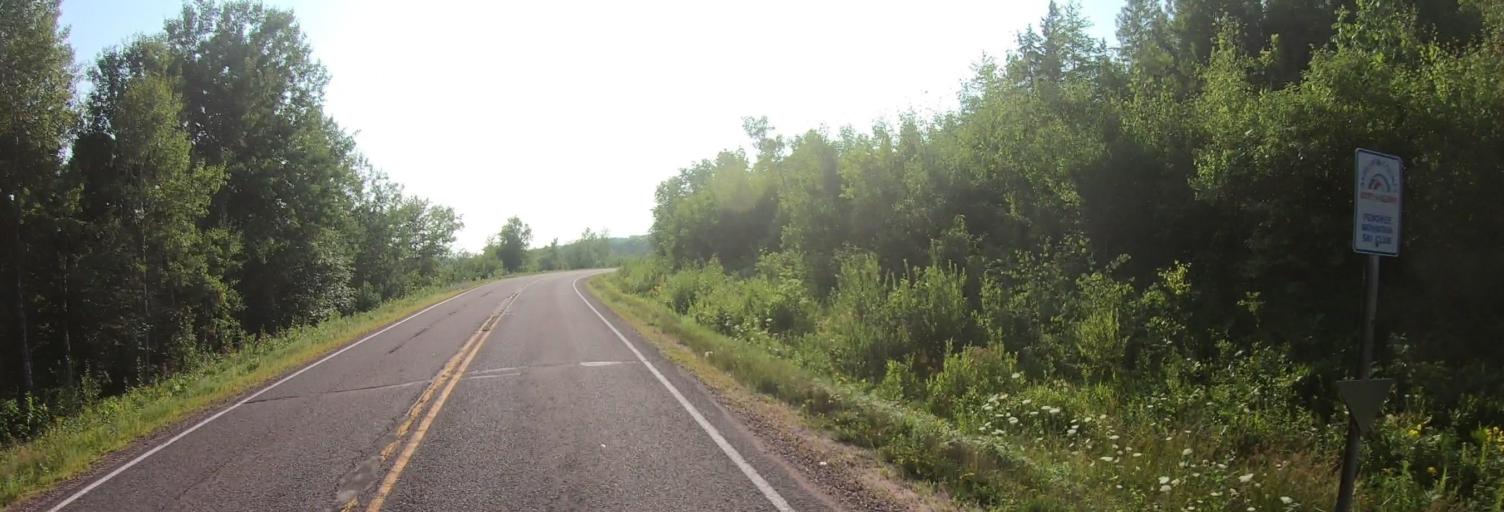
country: US
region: Wisconsin
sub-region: Ashland County
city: Ashland
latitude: 46.3197
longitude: -90.6732
